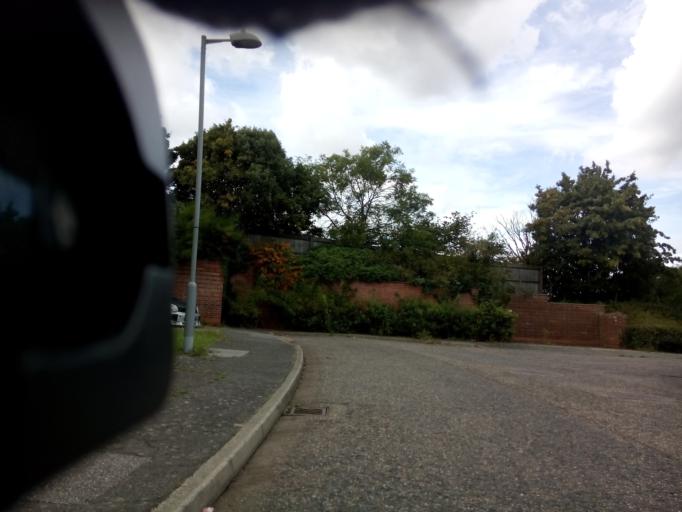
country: GB
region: England
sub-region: Suffolk
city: Ipswich
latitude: 52.0534
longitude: 1.1261
